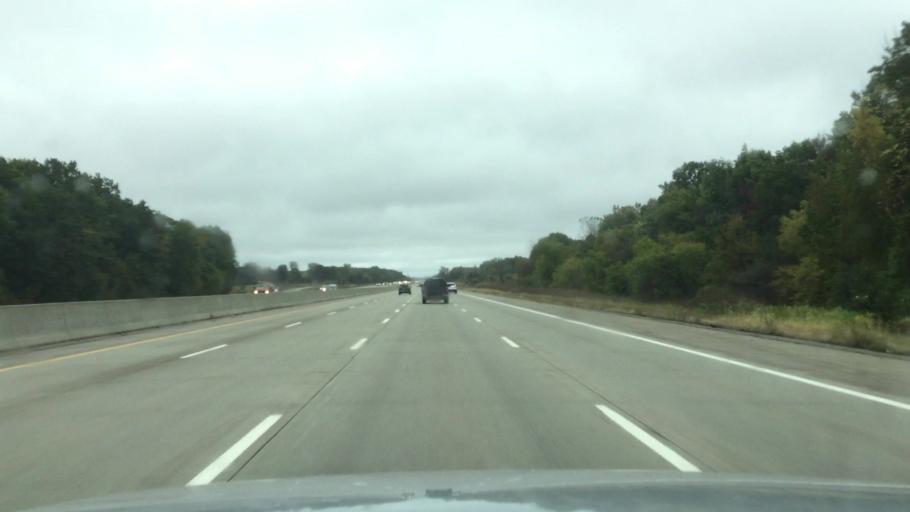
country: US
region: Michigan
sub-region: Saginaw County
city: Birch Run
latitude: 43.2855
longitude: -83.8117
